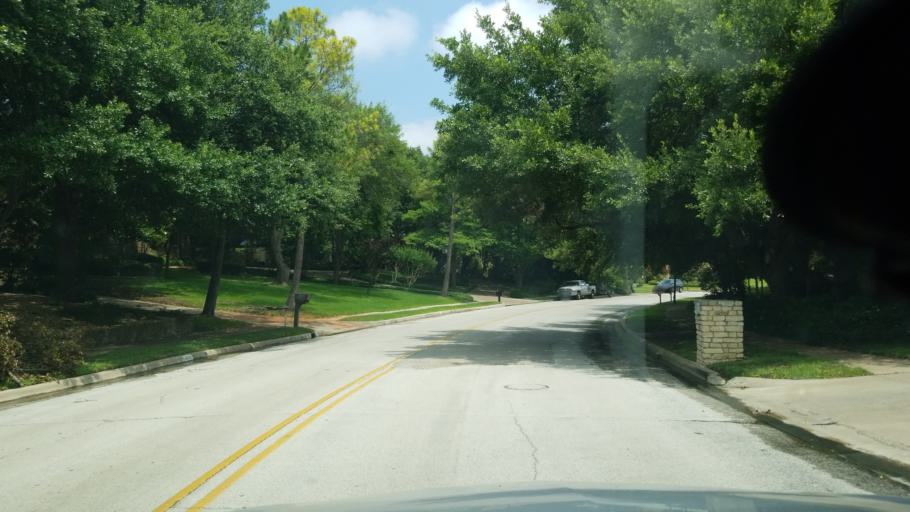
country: US
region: Texas
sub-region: Dallas County
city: Irving
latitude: 32.8560
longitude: -96.9423
